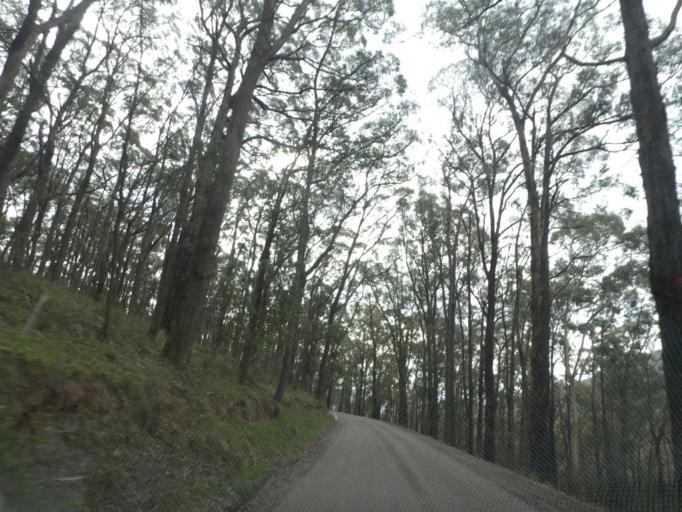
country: AU
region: Victoria
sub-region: Yarra Ranges
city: Olinda
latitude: -37.8524
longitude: 145.3463
